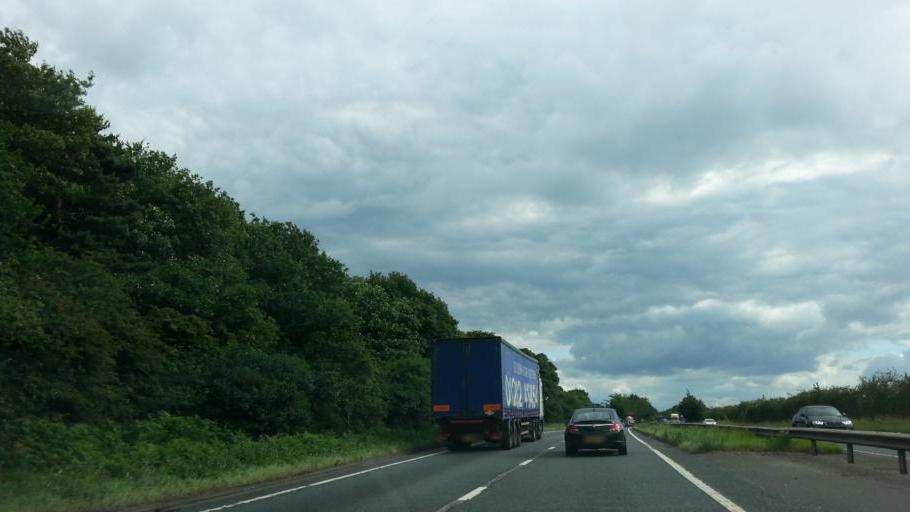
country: GB
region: England
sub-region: Nottinghamshire
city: Babworth
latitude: 53.3090
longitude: -1.0298
